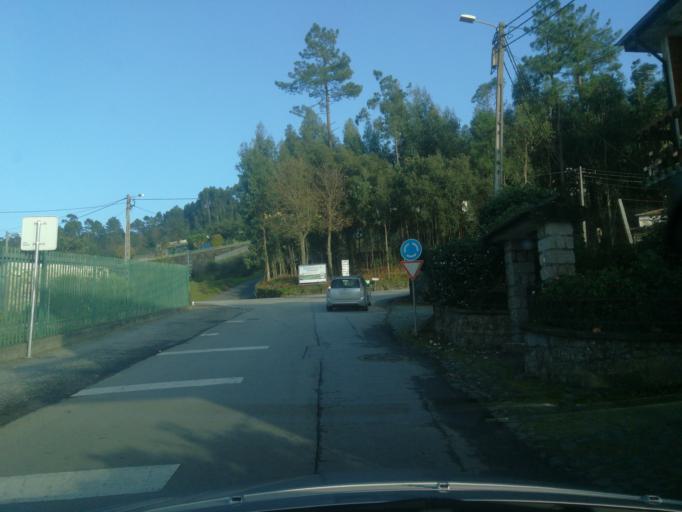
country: PT
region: Braga
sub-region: Barcelos
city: Galegos
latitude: 41.5142
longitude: -8.5610
